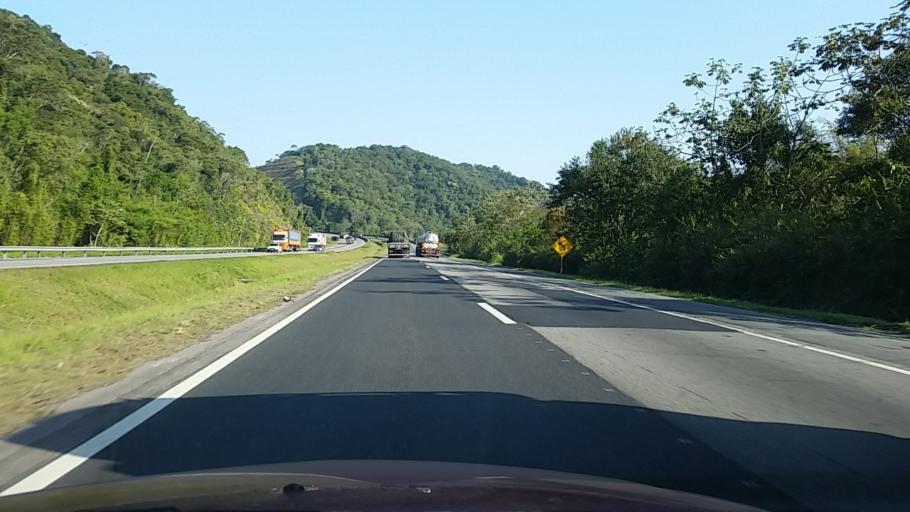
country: BR
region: Sao Paulo
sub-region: Miracatu
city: Miracatu
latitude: -24.2220
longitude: -47.3651
